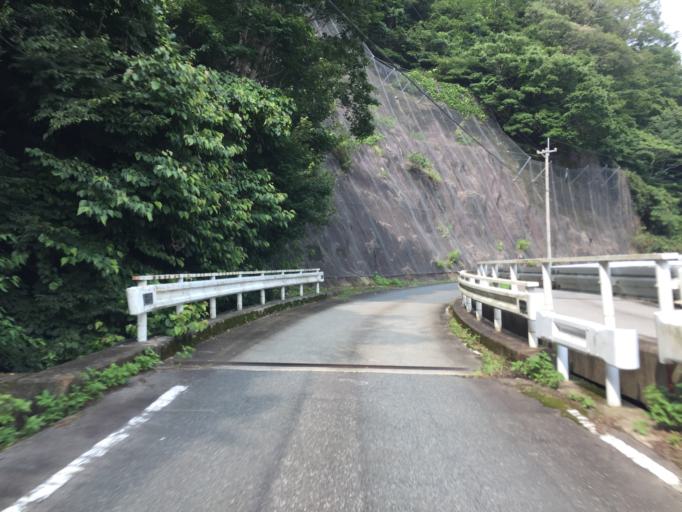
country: JP
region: Fukushima
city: Namie
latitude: 37.6005
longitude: 140.9019
